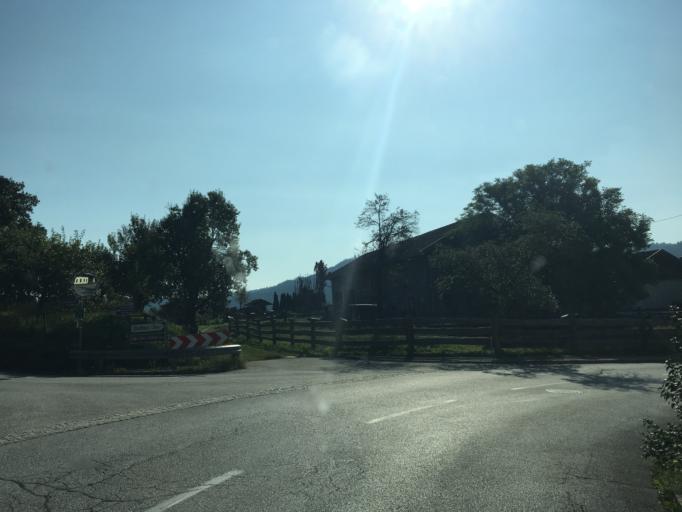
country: AT
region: Carinthia
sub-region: Politischer Bezirk Volkermarkt
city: Griffen
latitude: 46.6918
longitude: 14.7007
